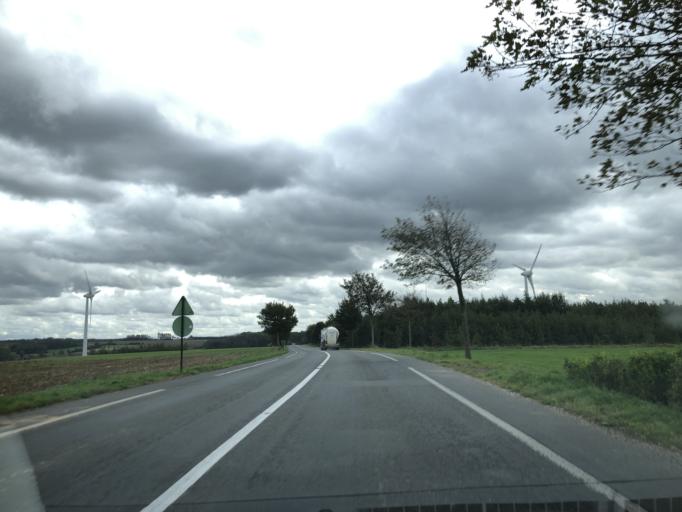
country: FR
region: Nord-Pas-de-Calais
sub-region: Departement du Pas-de-Calais
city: Wailly
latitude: 50.5537
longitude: 2.0986
